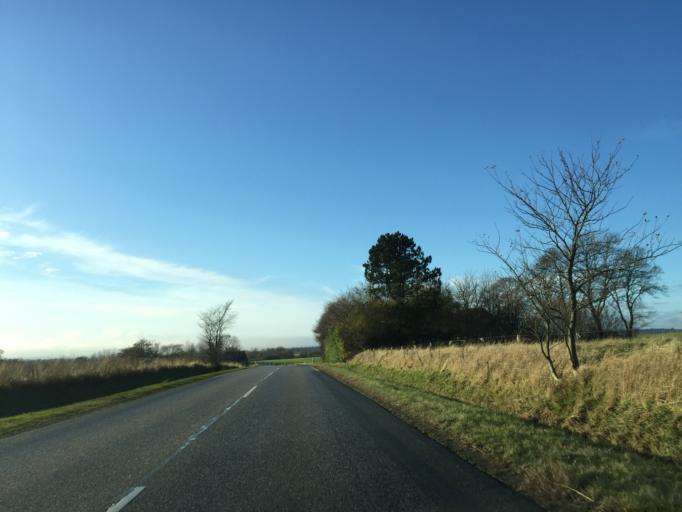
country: DK
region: Central Jutland
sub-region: Skanderborg Kommune
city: Galten
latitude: 56.1816
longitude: 9.9244
